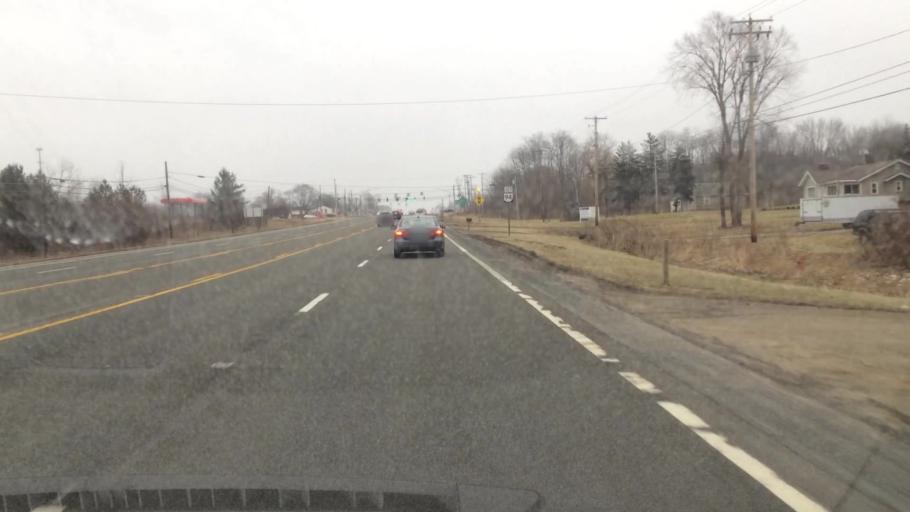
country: US
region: Ohio
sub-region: Summit County
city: Montrose-Ghent
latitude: 41.1361
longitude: -81.7390
